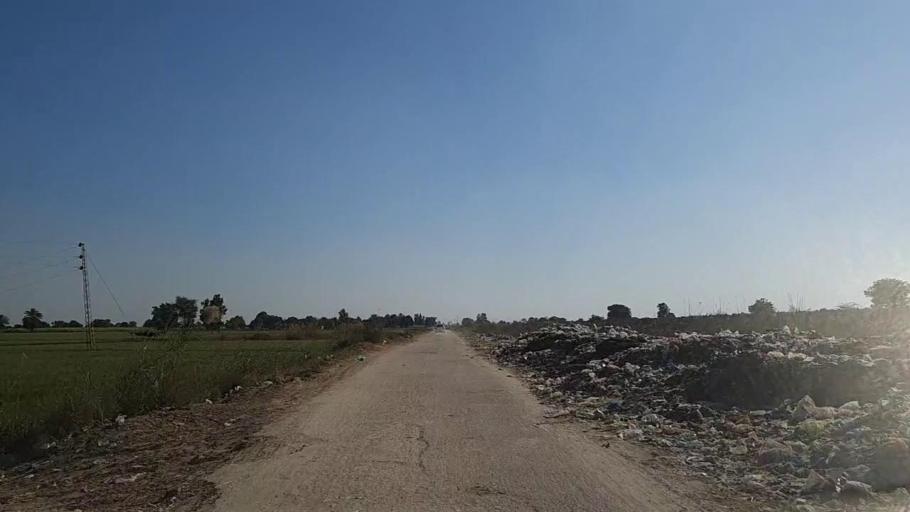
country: PK
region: Sindh
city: Nawabshah
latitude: 26.2358
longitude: 68.4254
